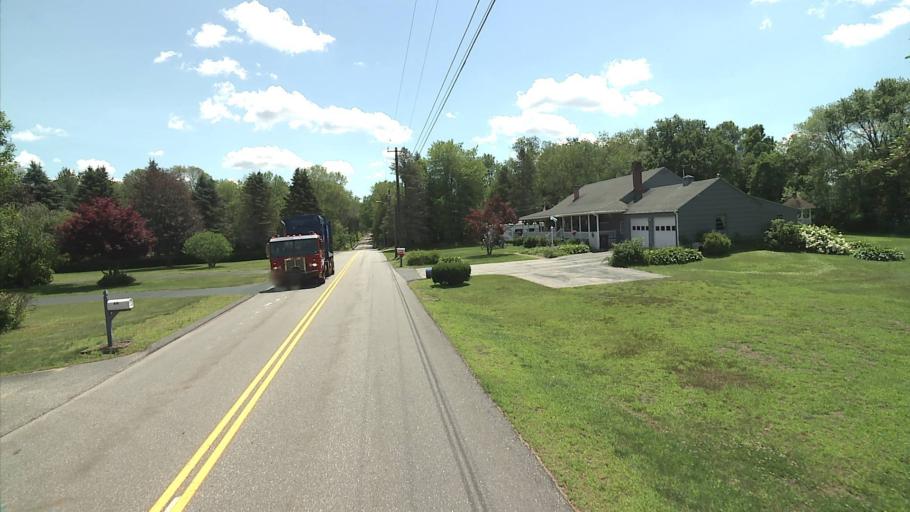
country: US
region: Connecticut
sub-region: New London County
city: Jewett City
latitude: 41.6100
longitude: -71.9298
